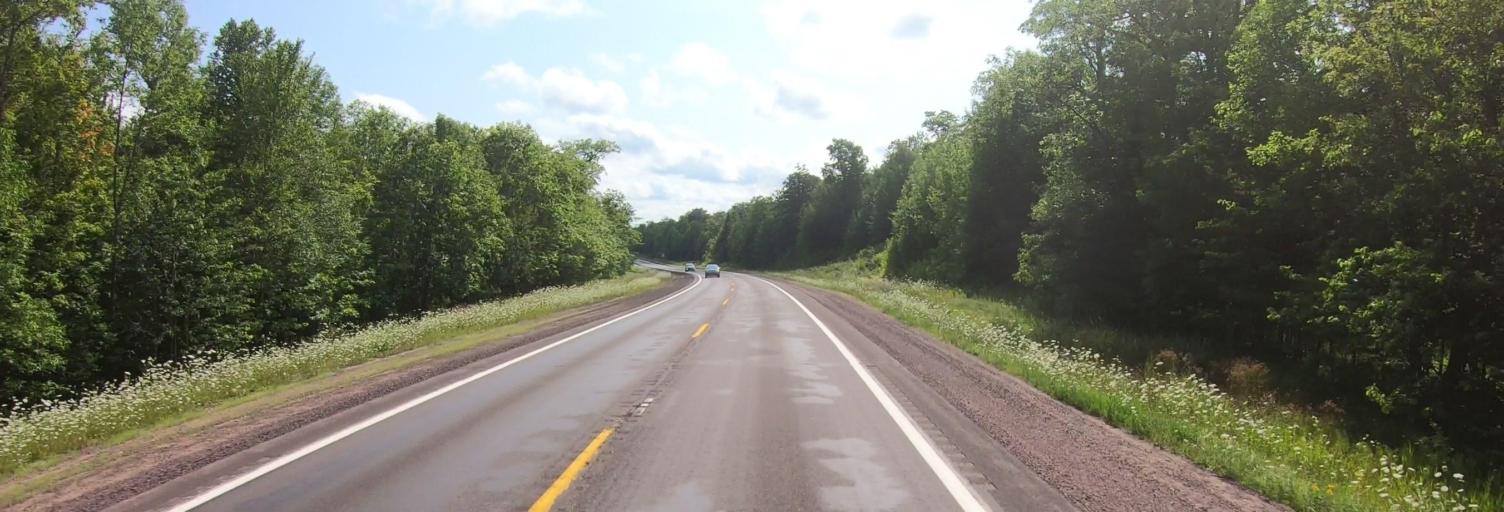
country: US
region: Michigan
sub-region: Ontonagon County
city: Ontonagon
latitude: 46.8377
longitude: -88.9915
